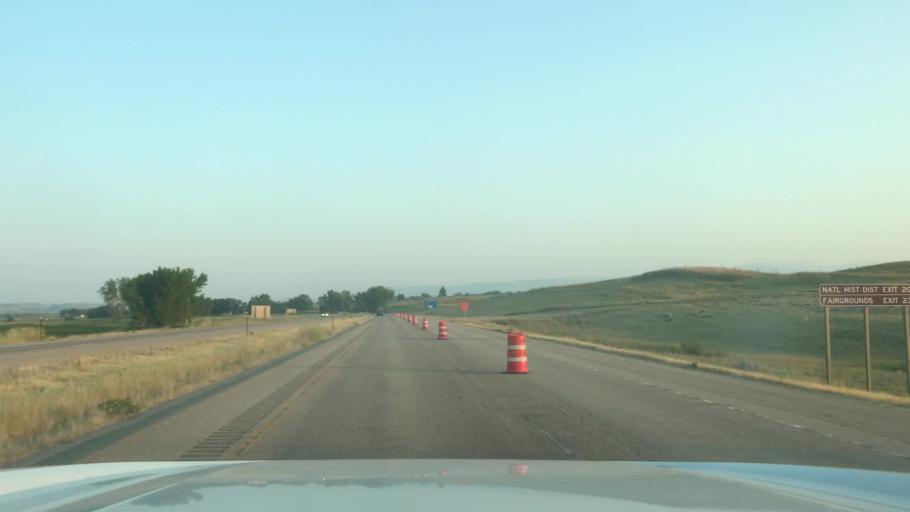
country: US
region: Wyoming
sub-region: Sheridan County
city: Sheridan
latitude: 44.8542
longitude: -106.9893
